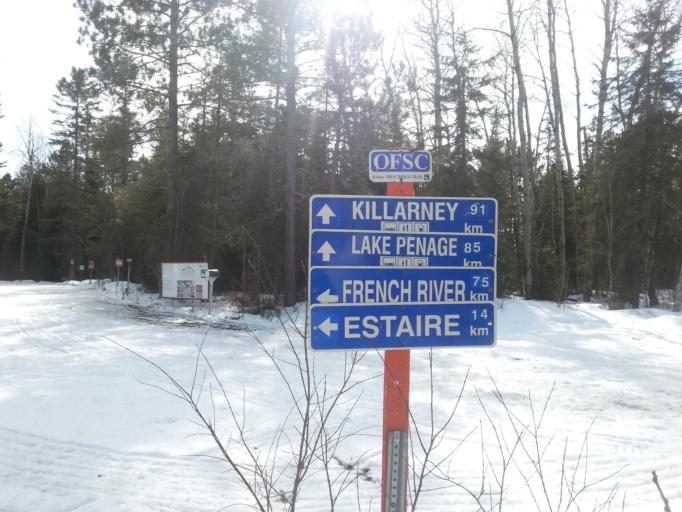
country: CA
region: Ontario
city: Greater Sudbury
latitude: 46.3443
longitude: -80.9020
